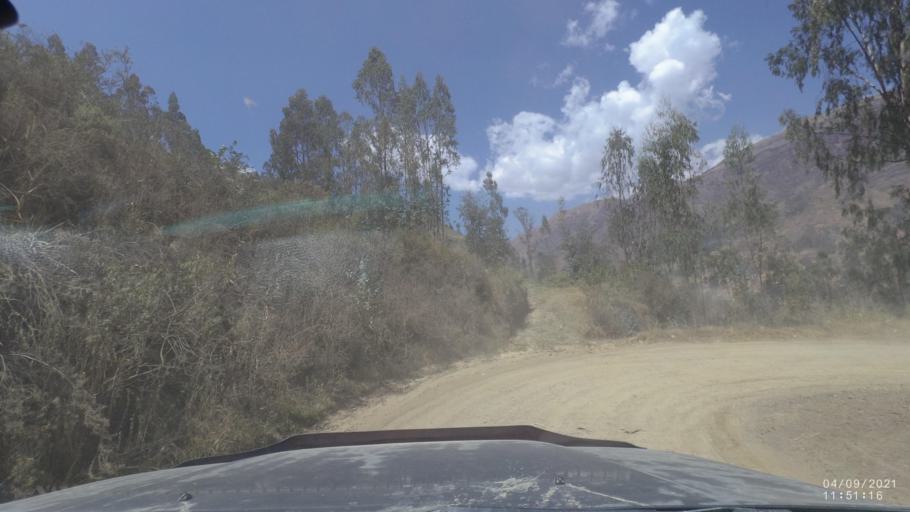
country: BO
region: Cochabamba
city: Colchani
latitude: -17.2296
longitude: -66.5259
